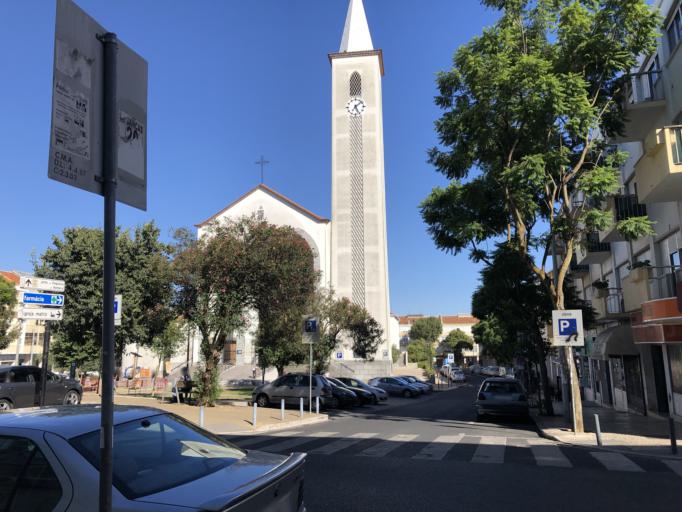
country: PT
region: Lisbon
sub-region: Amadora
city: Amadora
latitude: 38.7573
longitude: -9.2399
